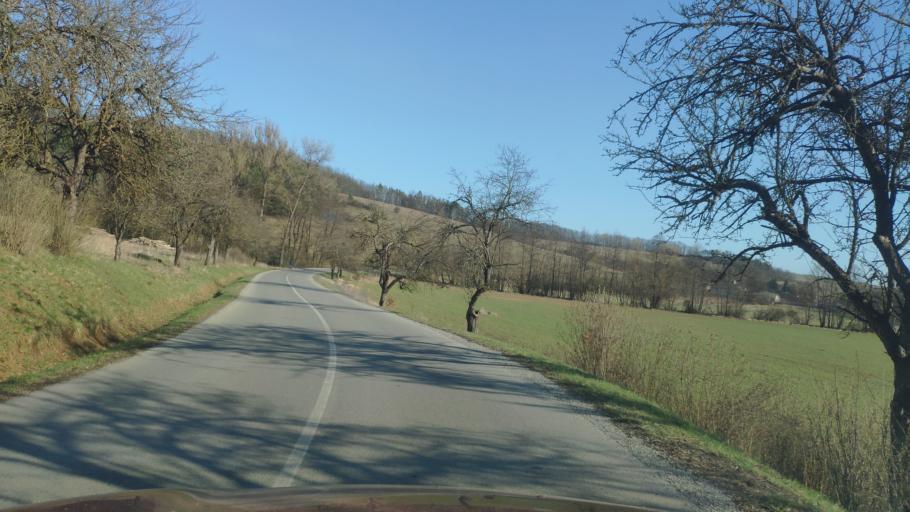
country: SK
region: Banskobystricky
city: Revuca
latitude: 48.5188
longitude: 20.2541
